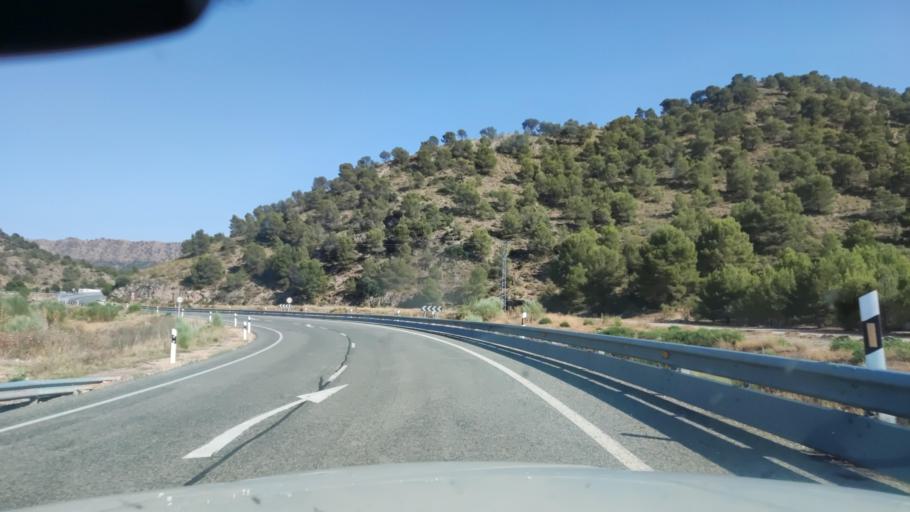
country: ES
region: Castille-La Mancha
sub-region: Provincia de Albacete
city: Tobarra
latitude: 38.6715
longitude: -1.6704
